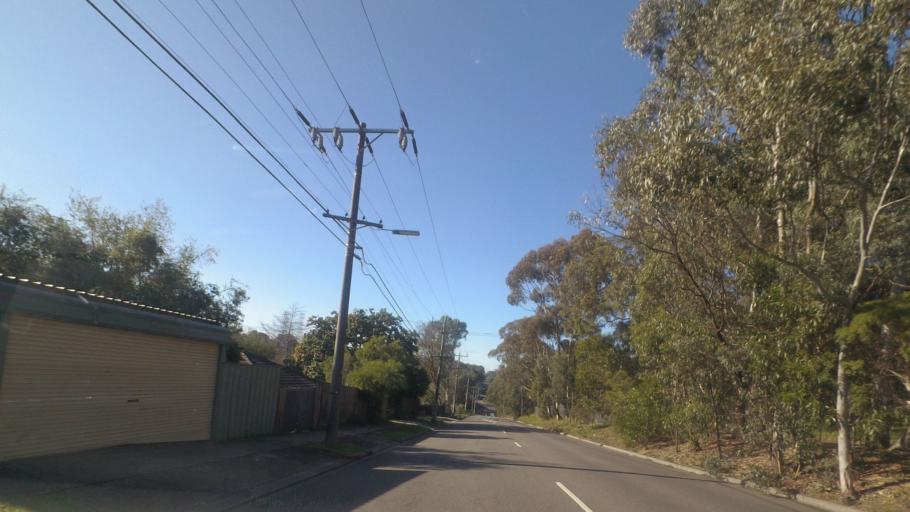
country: AU
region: Victoria
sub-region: Banyule
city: Yallambie
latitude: -37.7208
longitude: 145.0928
